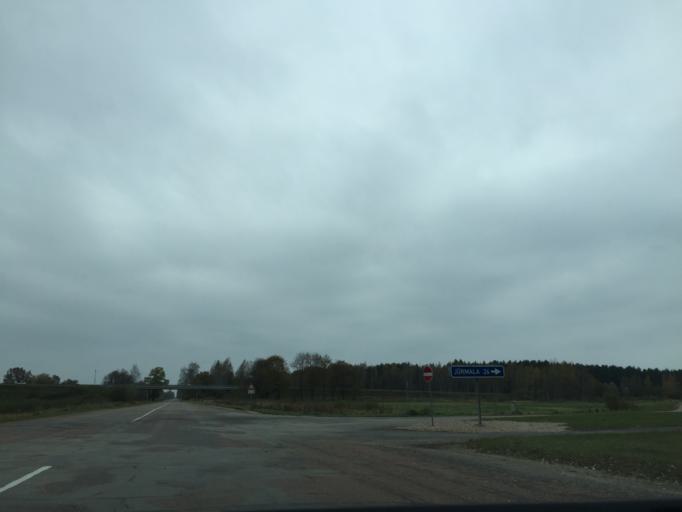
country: LV
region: Marupe
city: Marupe
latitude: 56.8387
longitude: 24.0374
